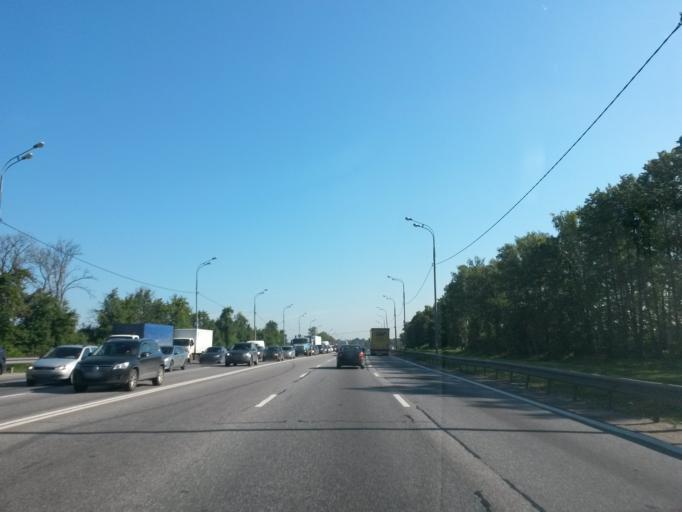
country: RU
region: Moskovskaya
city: Bolshevo
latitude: 55.9506
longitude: 37.8160
